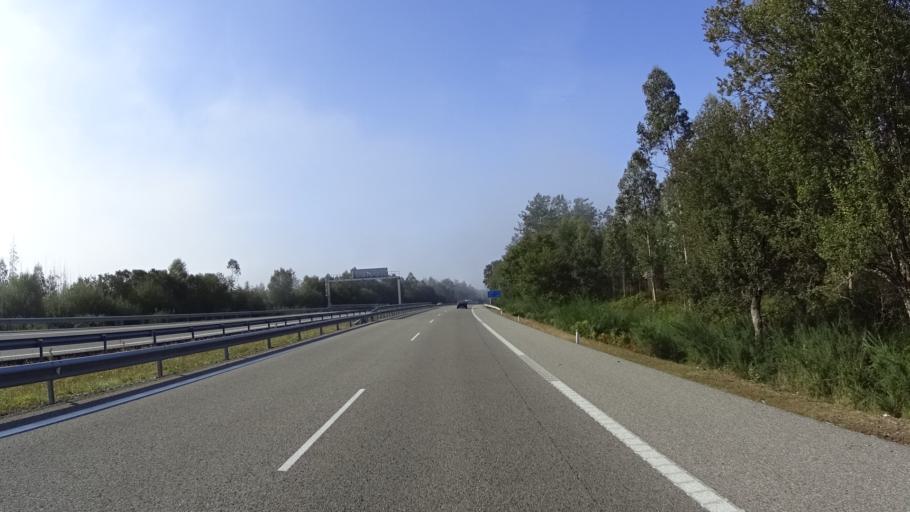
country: ES
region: Galicia
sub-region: Provincia da Coruna
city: Ordes
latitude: 43.0721
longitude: -8.3608
